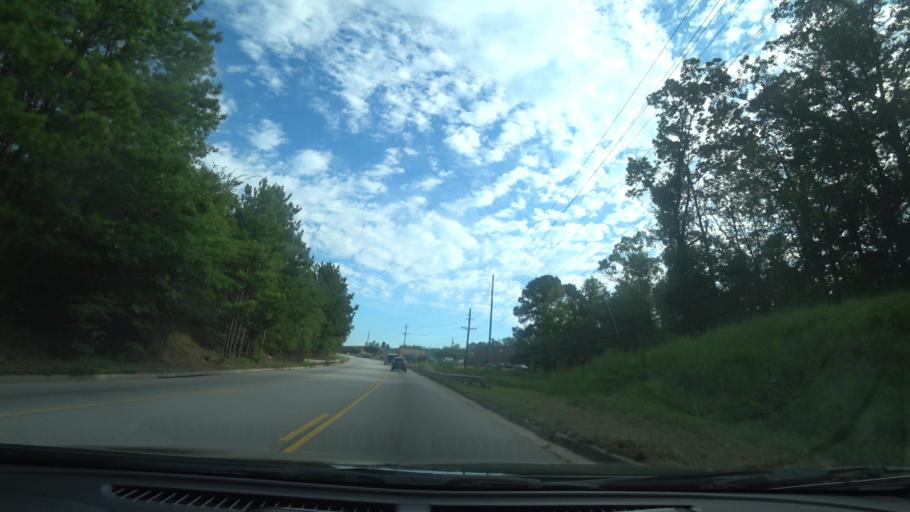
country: US
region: Georgia
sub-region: Rockdale County
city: Conyers
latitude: 33.6461
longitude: -83.9727
